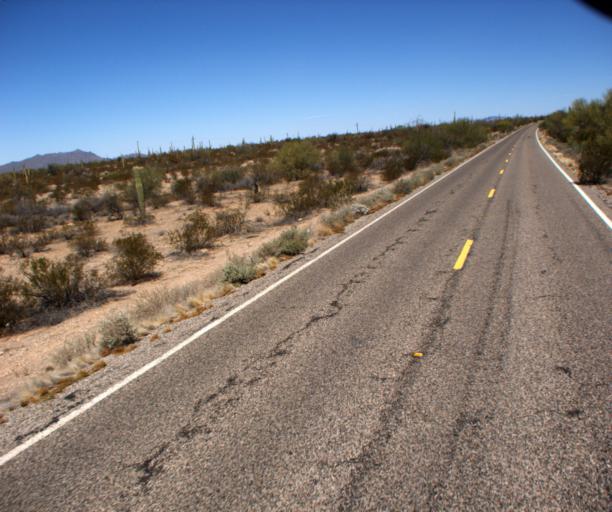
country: US
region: Arizona
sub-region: Pima County
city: Ajo
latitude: 32.2167
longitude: -112.7575
